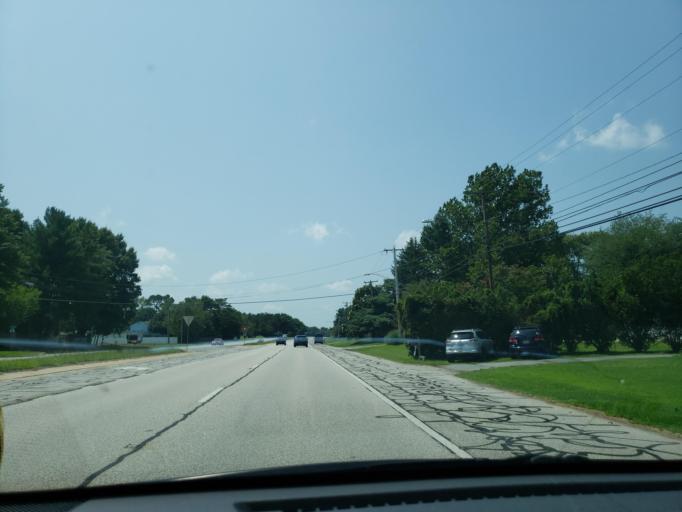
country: US
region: Delaware
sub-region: Kent County
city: Highland Acres
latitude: 39.1159
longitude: -75.5251
